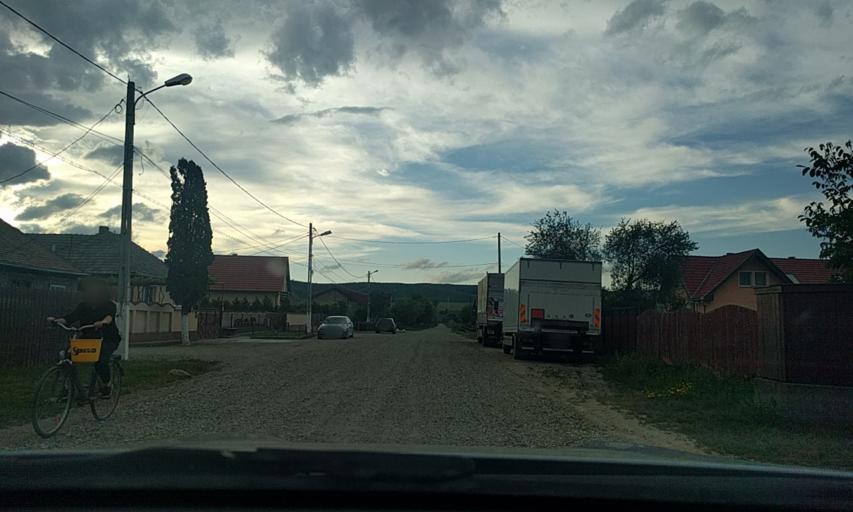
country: RO
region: Covasna
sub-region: Comuna Ilieni
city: Ilieni
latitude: 45.7617
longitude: 25.7222
